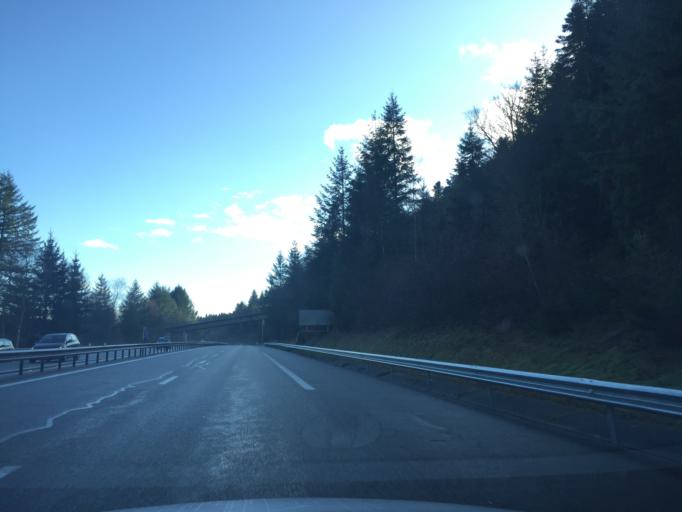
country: FR
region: Auvergne
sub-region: Departement du Puy-de-Dome
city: Chabreloche
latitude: 45.8535
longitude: 3.7264
